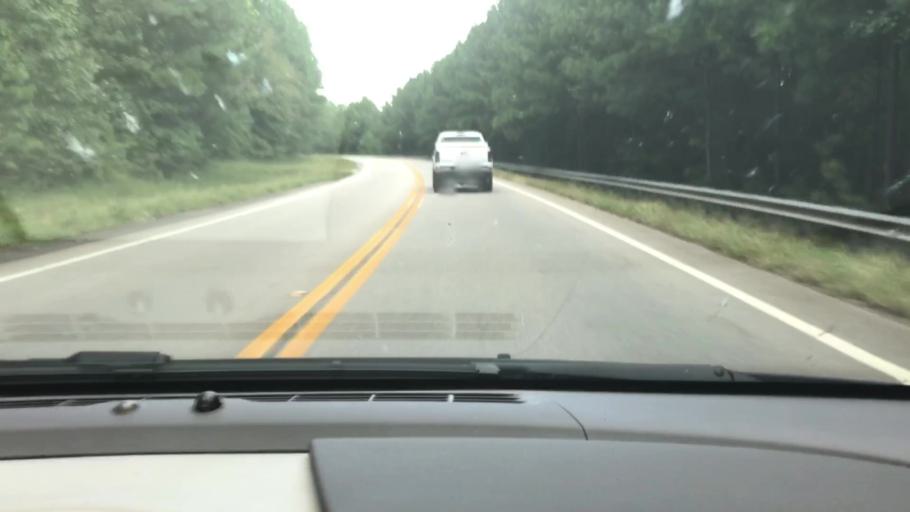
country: US
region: Georgia
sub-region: Troup County
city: La Grange
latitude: 32.9690
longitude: -85.0239
